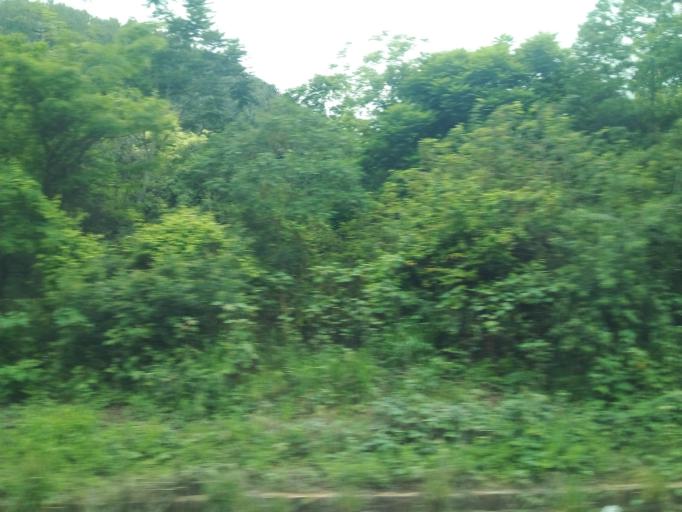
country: BR
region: Minas Gerais
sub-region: Rio Piracicaba
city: Rio Piracicaba
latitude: -19.9729
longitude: -43.2395
